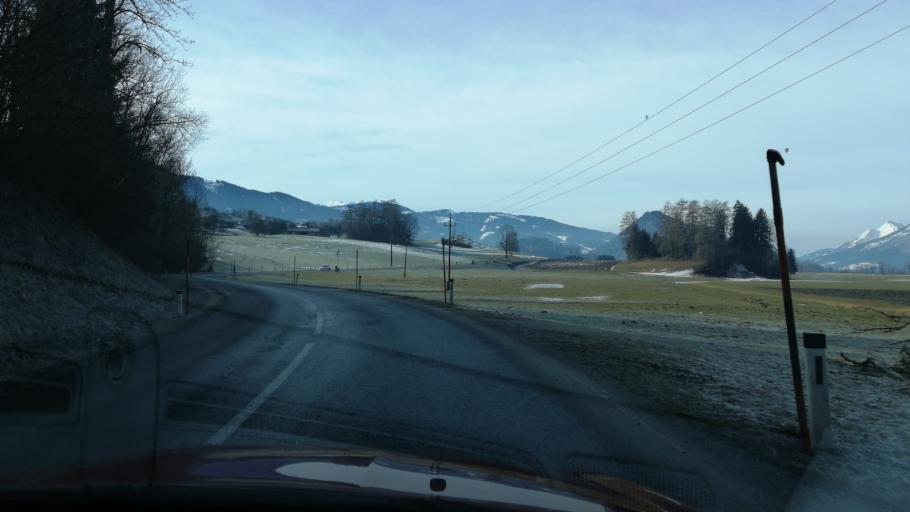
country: AT
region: Styria
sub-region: Politischer Bezirk Liezen
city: Worschach
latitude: 47.5396
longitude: 14.1648
